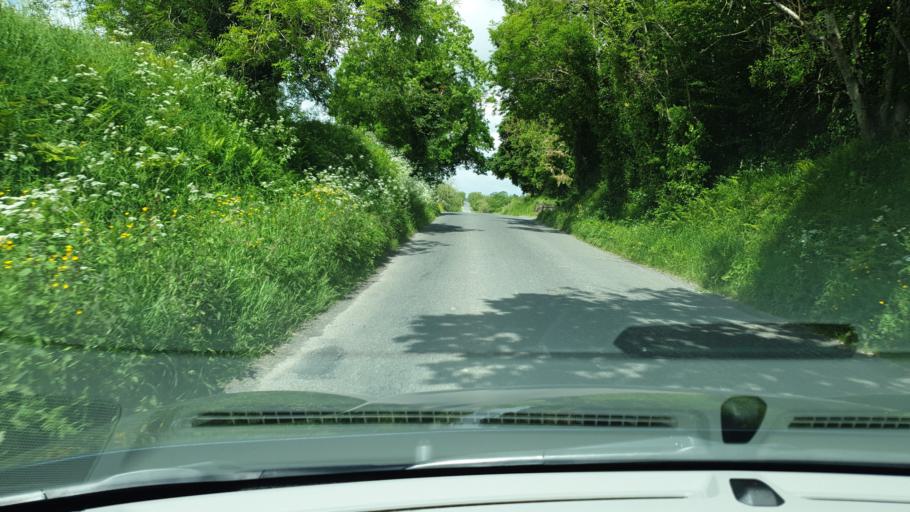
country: IE
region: Leinster
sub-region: An Mhi
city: Slane
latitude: 53.7252
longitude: -6.5422
